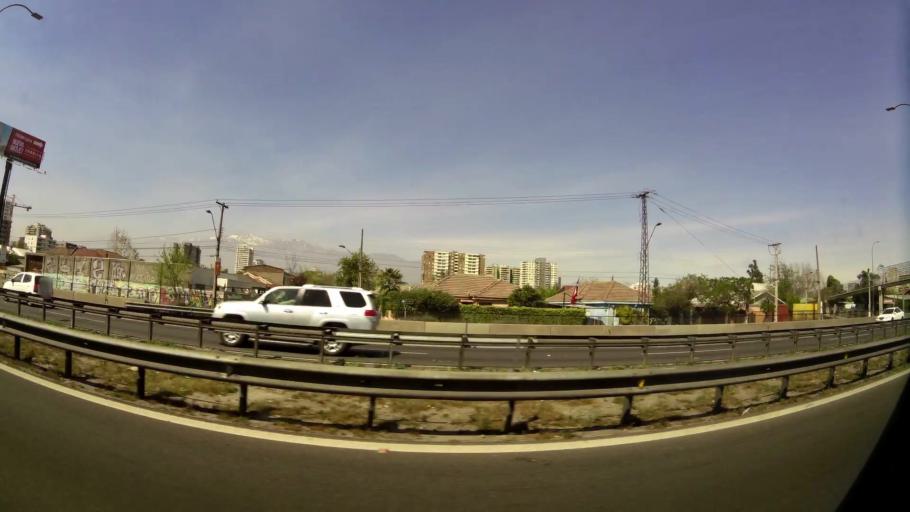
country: CL
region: Santiago Metropolitan
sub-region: Provincia de Santiago
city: Santiago
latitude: -33.4843
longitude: -70.6587
